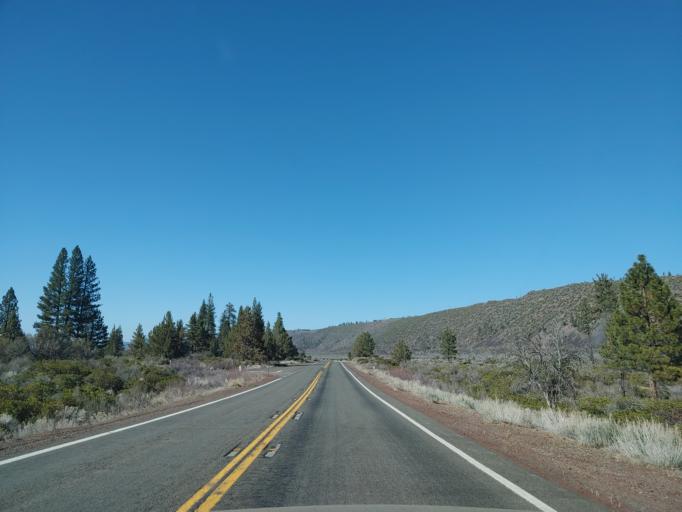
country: US
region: California
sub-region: Shasta County
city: Burney
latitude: 40.6913
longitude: -121.4199
